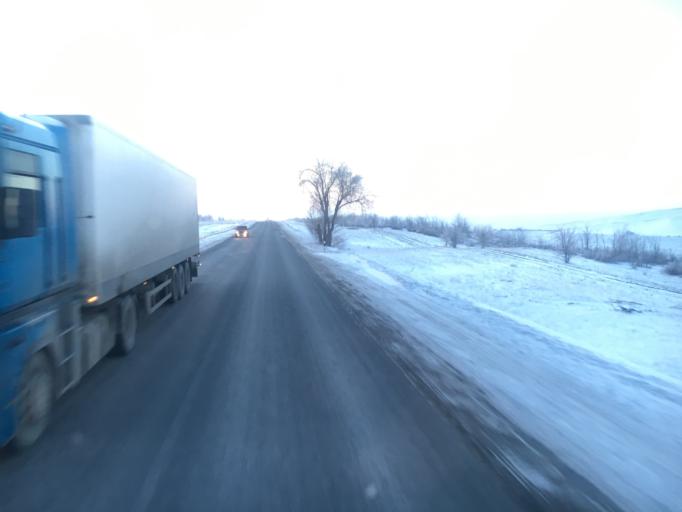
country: KZ
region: Aqtoebe
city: Aqtobe
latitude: 50.2831
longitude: 57.7408
